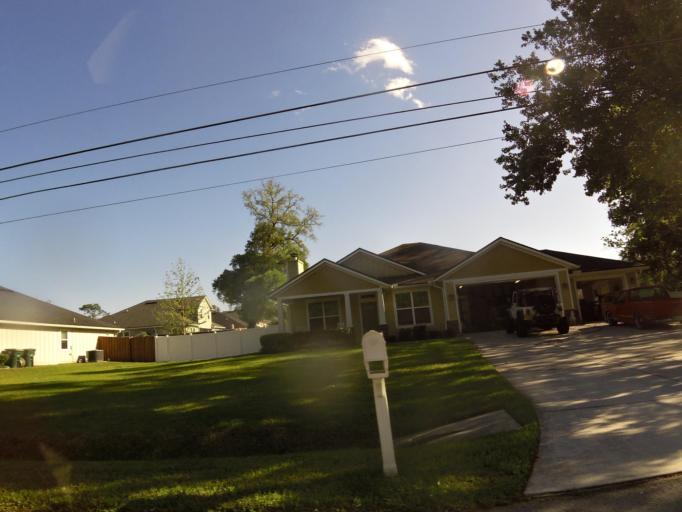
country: US
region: Florida
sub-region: Duval County
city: Jacksonville
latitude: 30.2741
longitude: -81.5765
